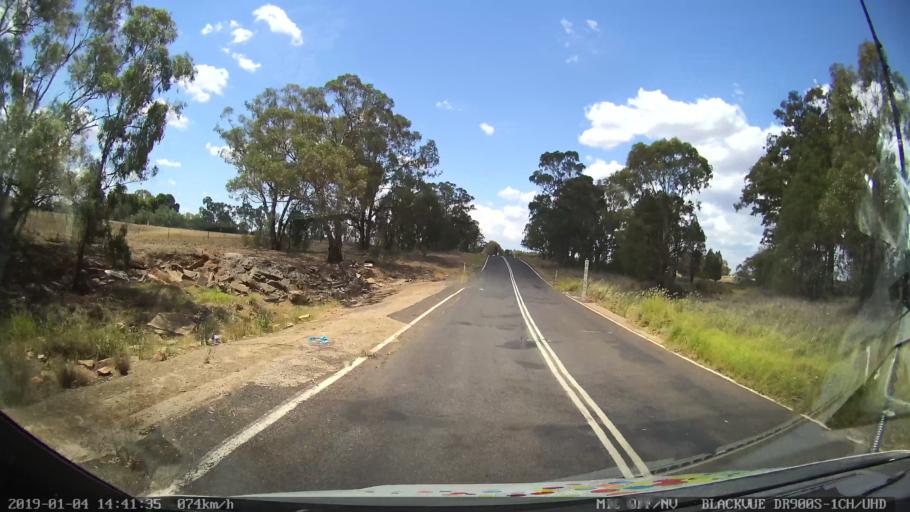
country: AU
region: New South Wales
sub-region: Dubbo Municipality
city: Dubbo
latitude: -32.1373
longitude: 148.6365
